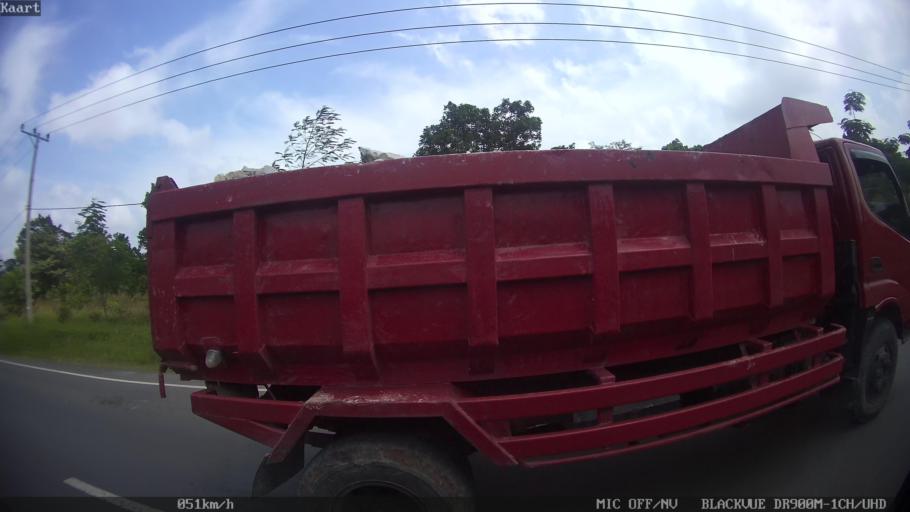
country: ID
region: Lampung
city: Kedaton
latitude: -5.3568
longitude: 105.3142
